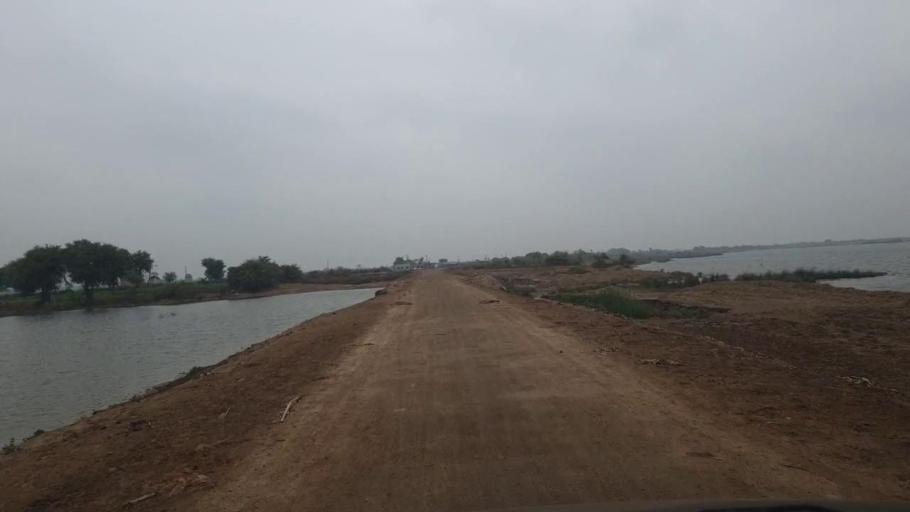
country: PK
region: Sindh
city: Tando Adam
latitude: 25.8482
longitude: 68.6944
